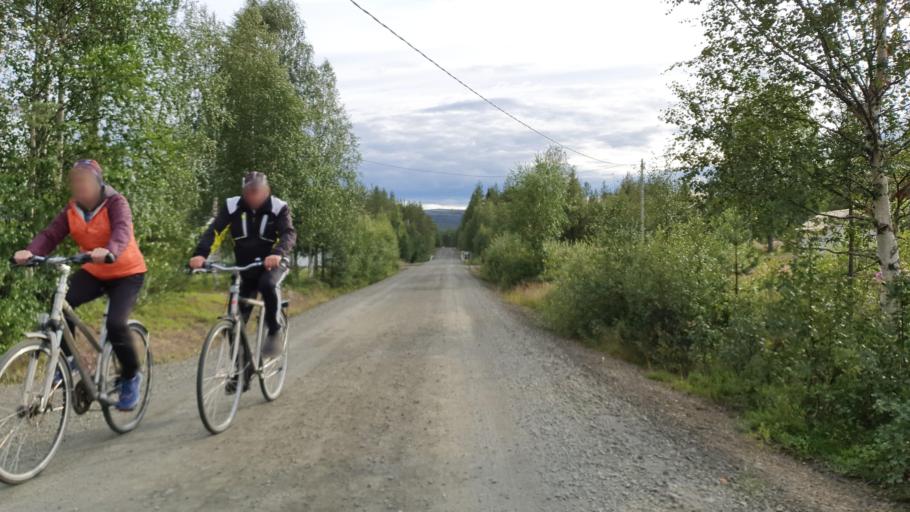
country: FI
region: Lapland
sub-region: Tunturi-Lappi
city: Kolari
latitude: 67.6232
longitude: 24.1642
